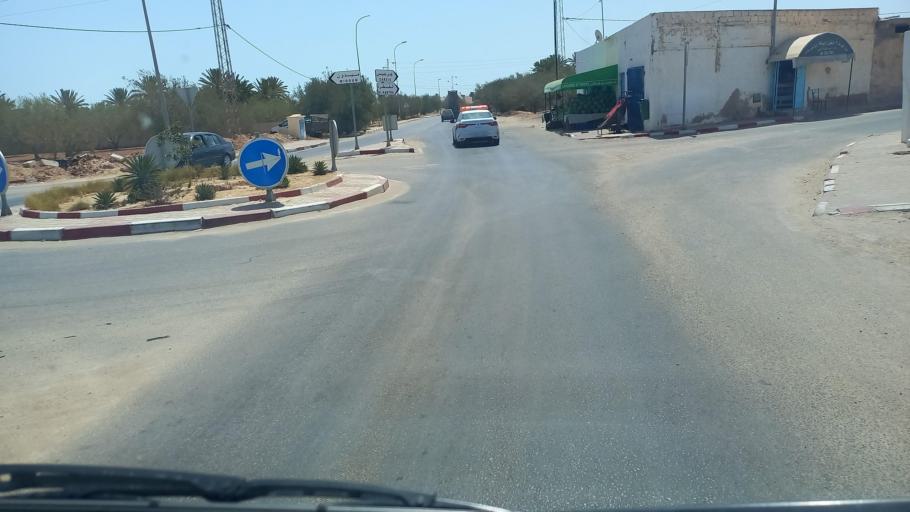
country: TN
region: Madanin
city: Midoun
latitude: 33.7746
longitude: 10.8958
